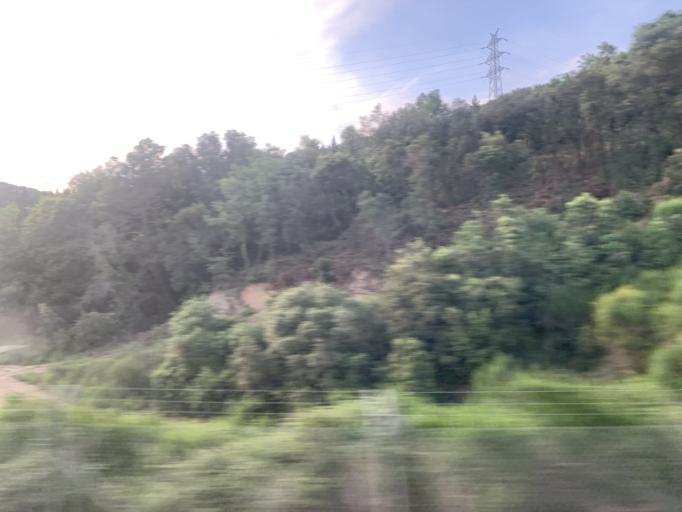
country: ES
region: Catalonia
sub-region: Provincia de Barcelona
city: Sant Celoni
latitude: 41.6959
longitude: 2.4891
